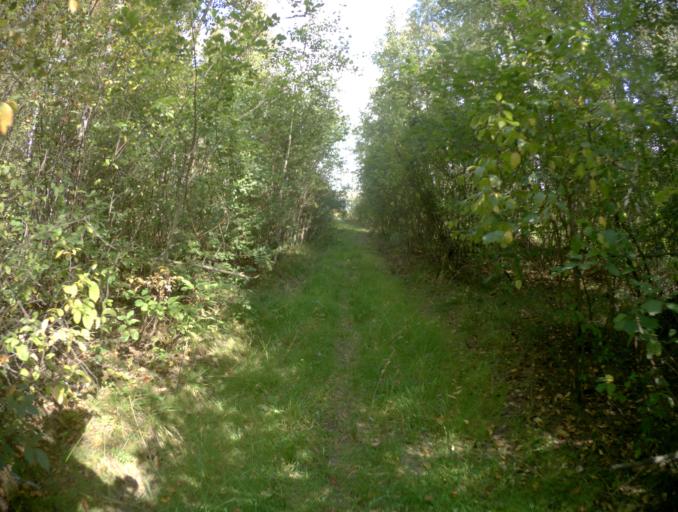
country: RU
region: Vladimir
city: Petushki
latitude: 55.8564
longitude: 39.3560
